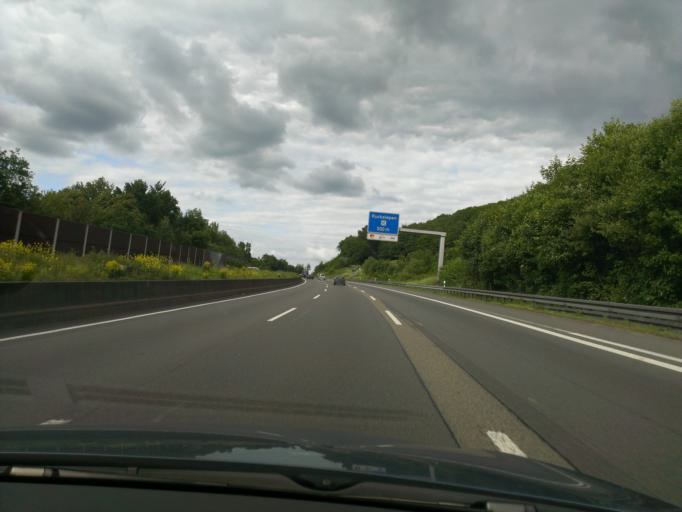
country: DE
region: North Rhine-Westphalia
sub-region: Regierungsbezirk Arnsberg
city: Schwelm
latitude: 51.2605
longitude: 7.2384
